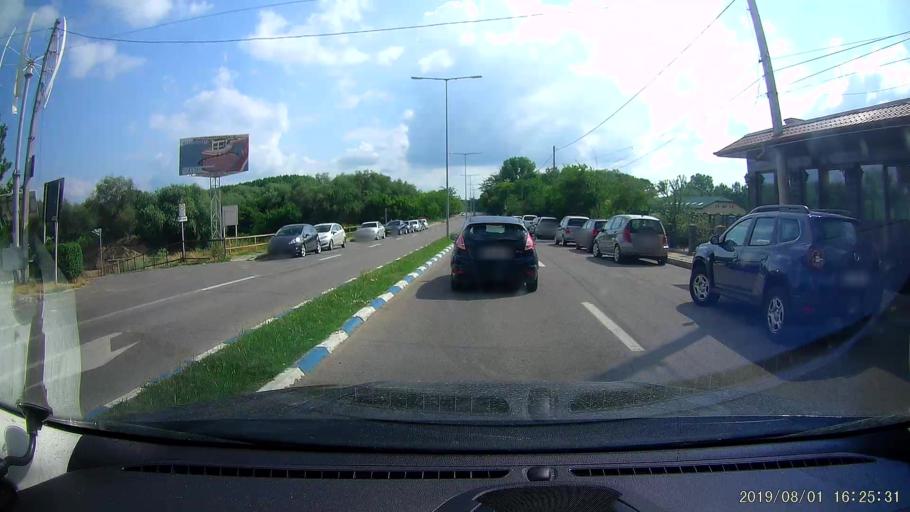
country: RO
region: Calarasi
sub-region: Municipiul Calarasi
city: Calarasi
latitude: 44.1915
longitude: 27.3257
